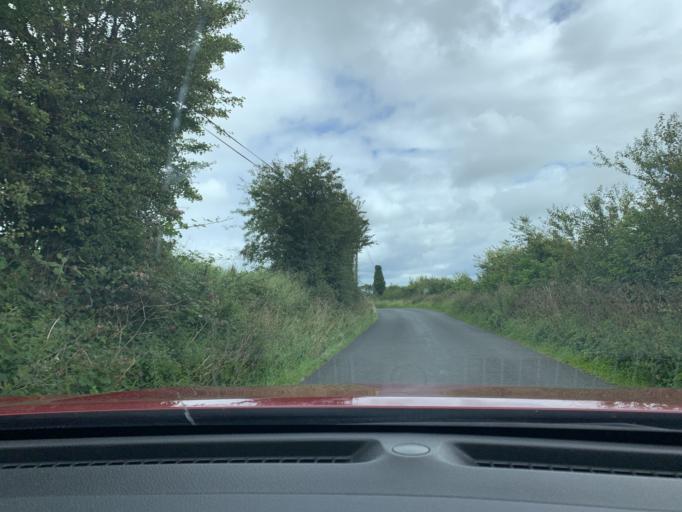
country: IE
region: Connaught
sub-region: County Leitrim
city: Carrick-on-Shannon
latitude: 53.8574
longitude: -8.1473
